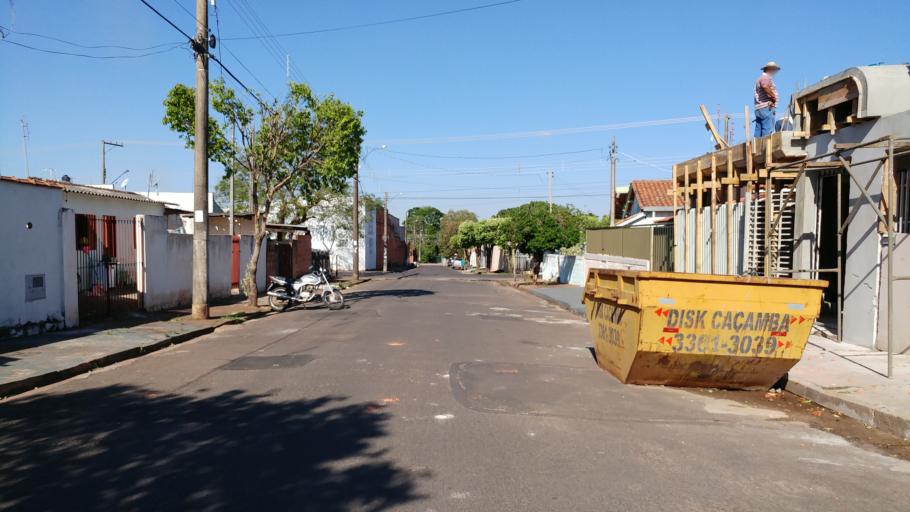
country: BR
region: Sao Paulo
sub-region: Paraguacu Paulista
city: Paraguacu Paulista
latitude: -22.4252
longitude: -50.5778
